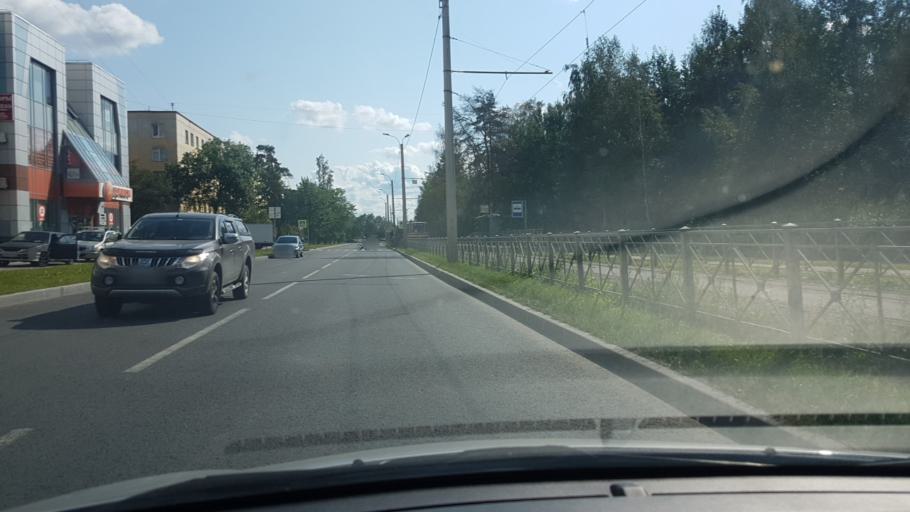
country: RU
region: St.-Petersburg
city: Sosnovaya Polyana
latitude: 59.8276
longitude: 30.1401
